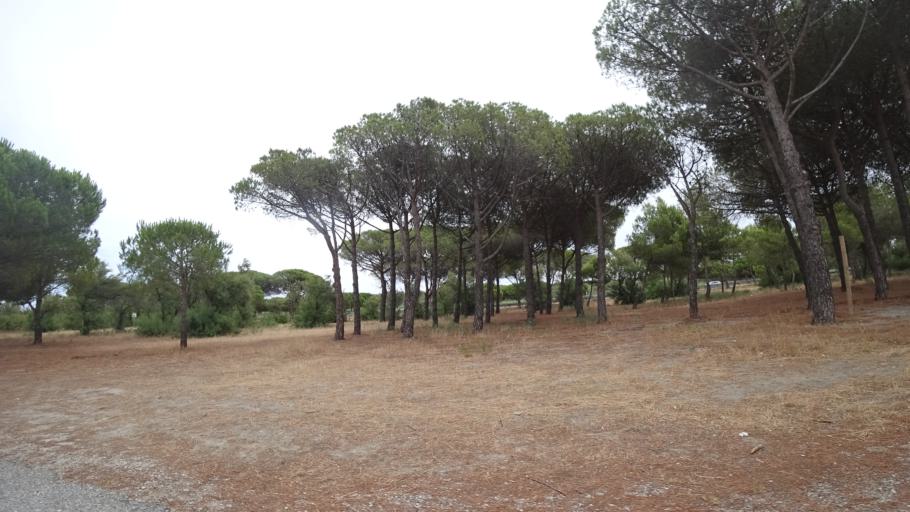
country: FR
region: Languedoc-Roussillon
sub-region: Departement des Pyrenees-Orientales
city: Le Barcares
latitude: 42.8182
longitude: 3.0296
